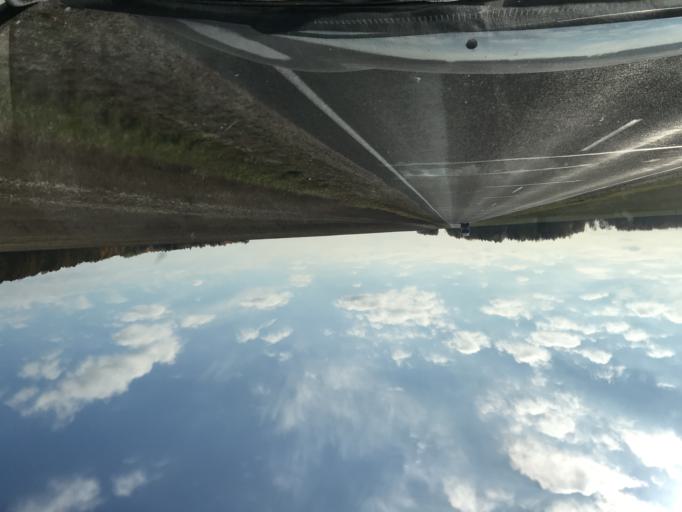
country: BY
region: Grodnenskaya
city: Voranava
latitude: 54.1968
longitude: 25.3463
